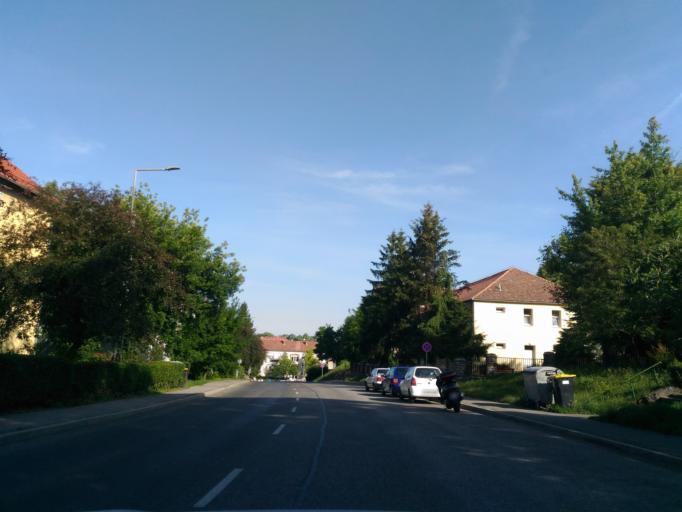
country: HU
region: Baranya
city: Komlo
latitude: 46.1840
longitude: 18.2584
